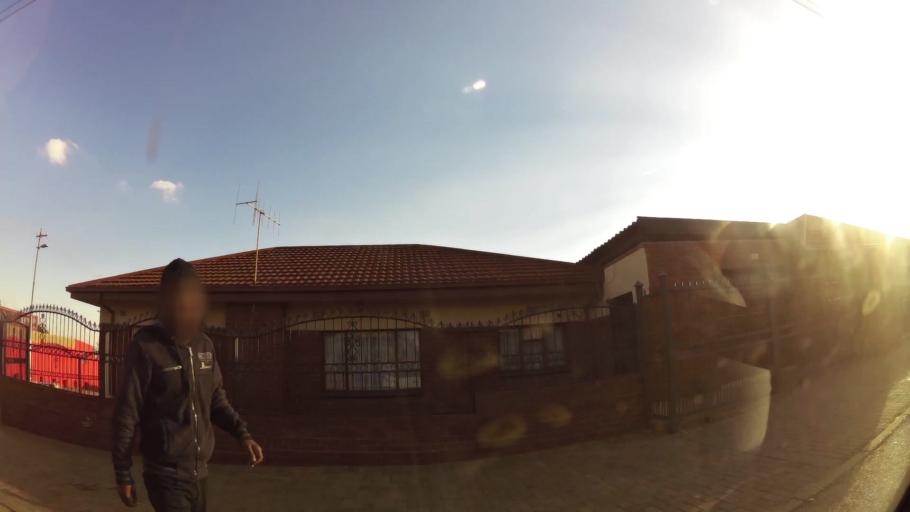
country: ZA
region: Gauteng
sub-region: City of Tshwane Metropolitan Municipality
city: Cullinan
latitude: -25.7050
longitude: 28.3895
